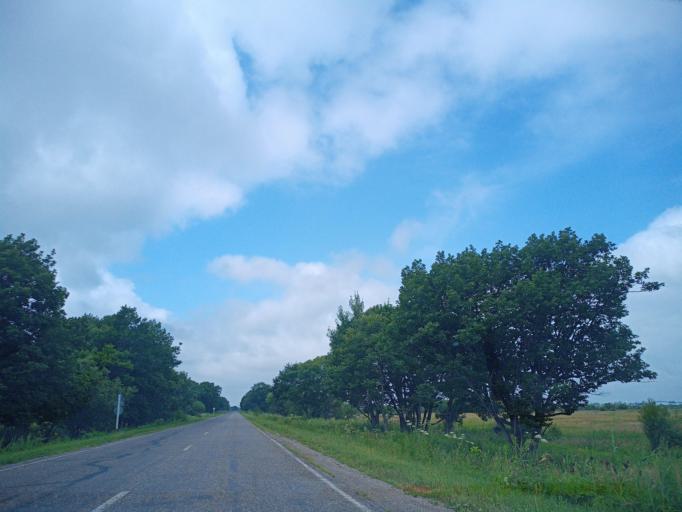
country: RU
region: Primorskiy
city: Dal'nerechensk
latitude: 45.9358
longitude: 133.8502
